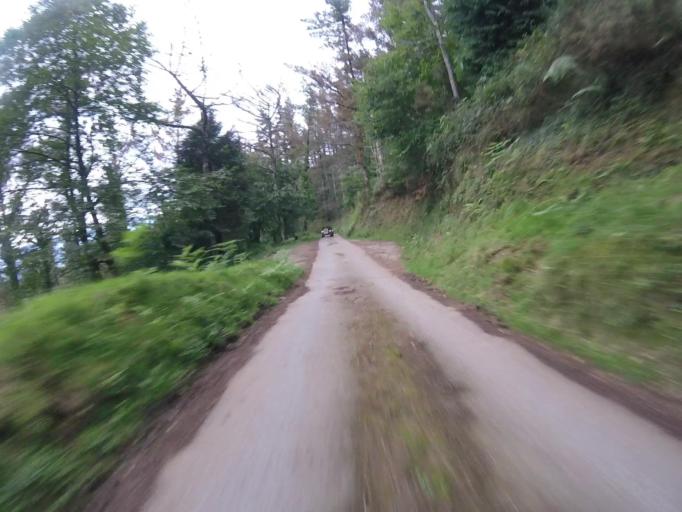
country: ES
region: Basque Country
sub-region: Provincia de Guipuzcoa
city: Errenteria
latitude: 43.2677
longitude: -1.8337
